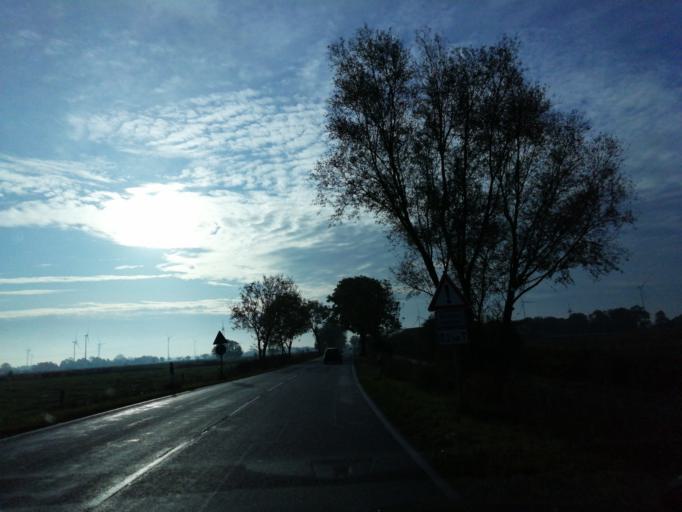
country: DE
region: Lower Saxony
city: Fedderwarden
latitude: 53.6220
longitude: 8.0337
